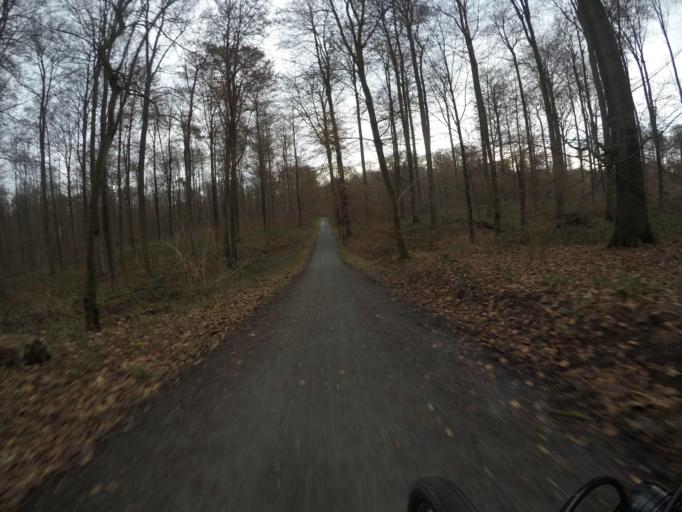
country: BE
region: Flanders
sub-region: Provincie Vlaams-Brabant
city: Hoeilaart
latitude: 50.7511
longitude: 4.4464
